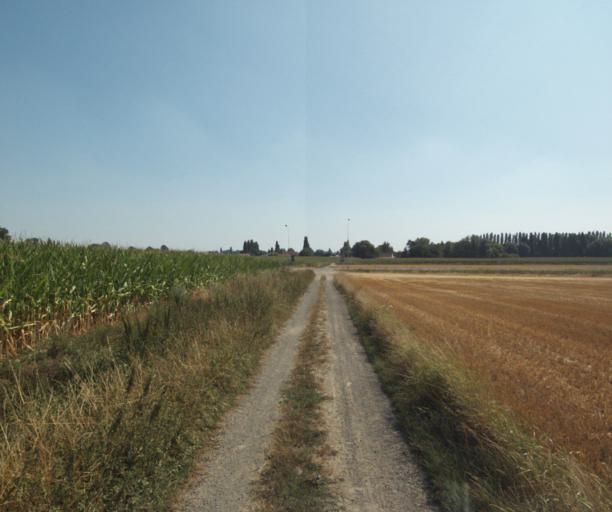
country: FR
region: Nord-Pas-de-Calais
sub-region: Departement du Nord
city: Linselles
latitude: 50.7566
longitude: 3.0626
